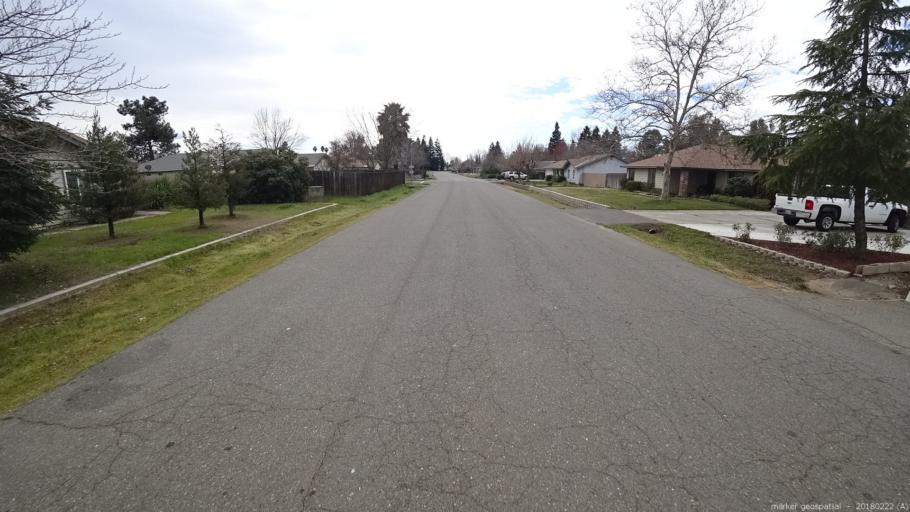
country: US
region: California
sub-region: Sacramento County
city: Rio Linda
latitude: 38.7200
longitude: -121.4121
